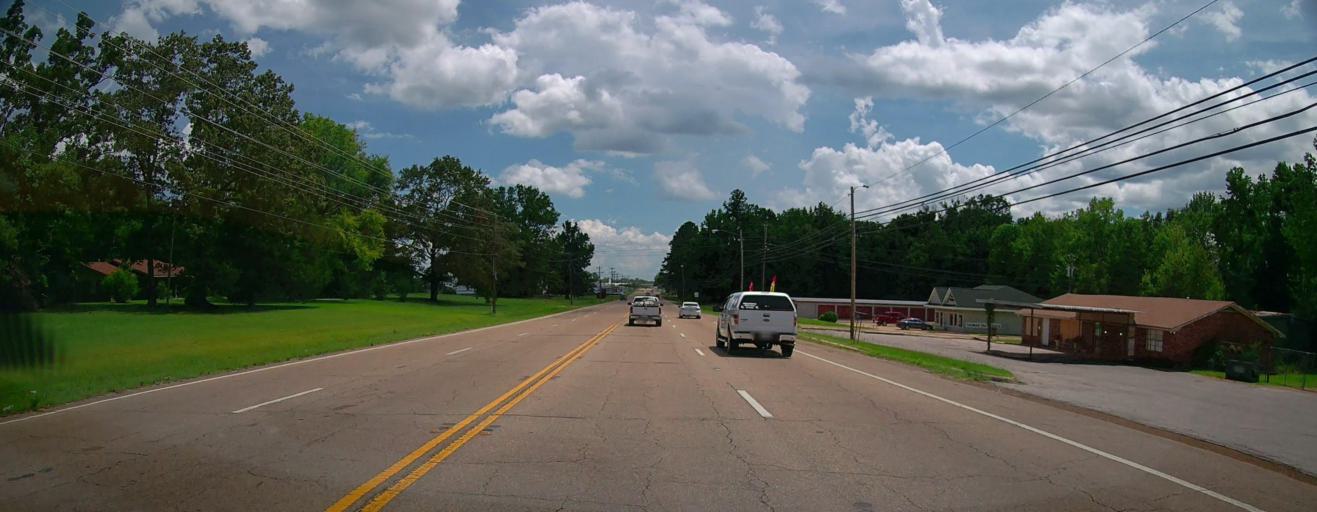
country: US
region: Mississippi
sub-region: Lee County
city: Verona
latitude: 34.1733
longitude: -88.7197
